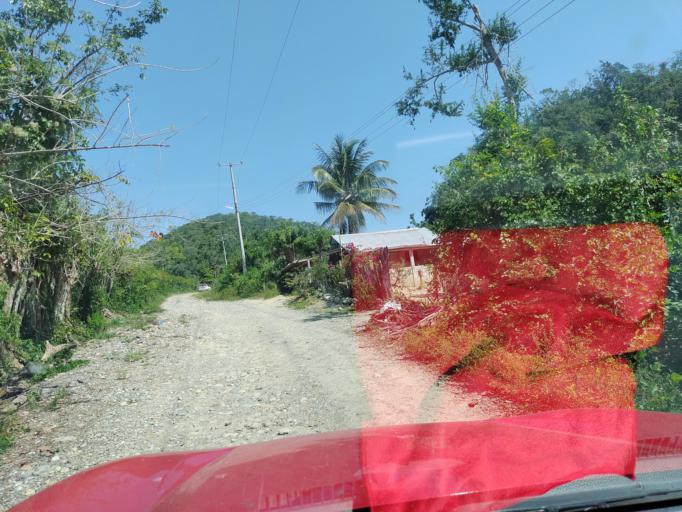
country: MX
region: Veracruz
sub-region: Papantla
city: Polutla
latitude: 20.5032
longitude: -97.2136
